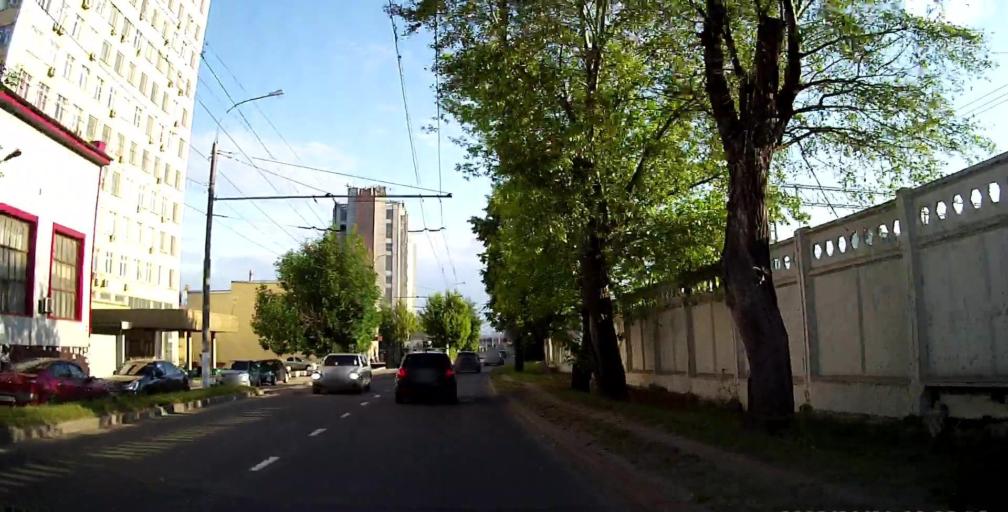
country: RU
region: Moskovskaya
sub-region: Podol'skiy Rayon
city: Podol'sk
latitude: 55.4300
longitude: 37.5655
